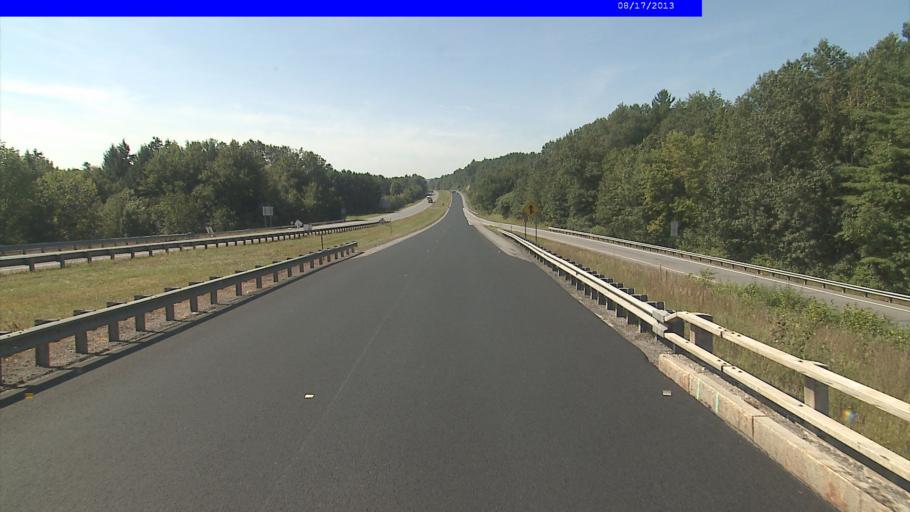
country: US
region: Vermont
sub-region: Windham County
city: Bellows Falls
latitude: 43.0910
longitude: -72.4566
